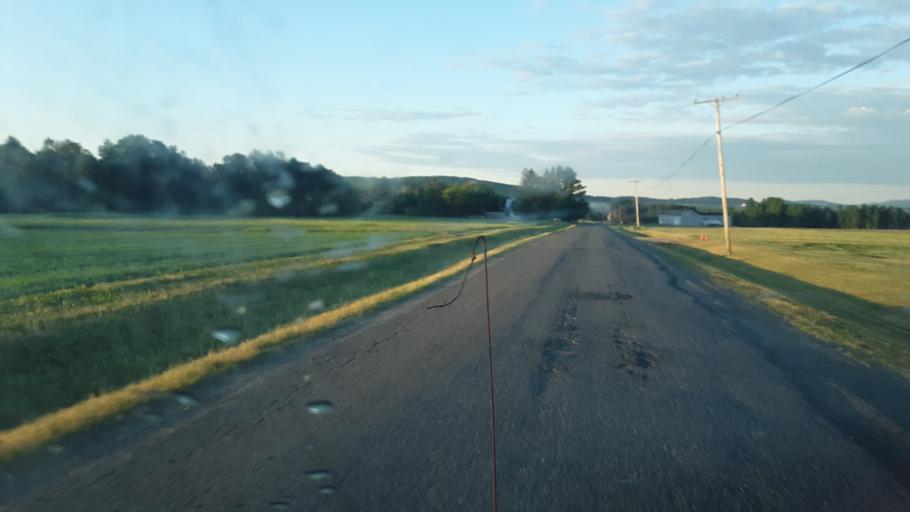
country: US
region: Maine
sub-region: Aroostook County
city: Presque Isle
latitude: 46.7687
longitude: -68.1021
